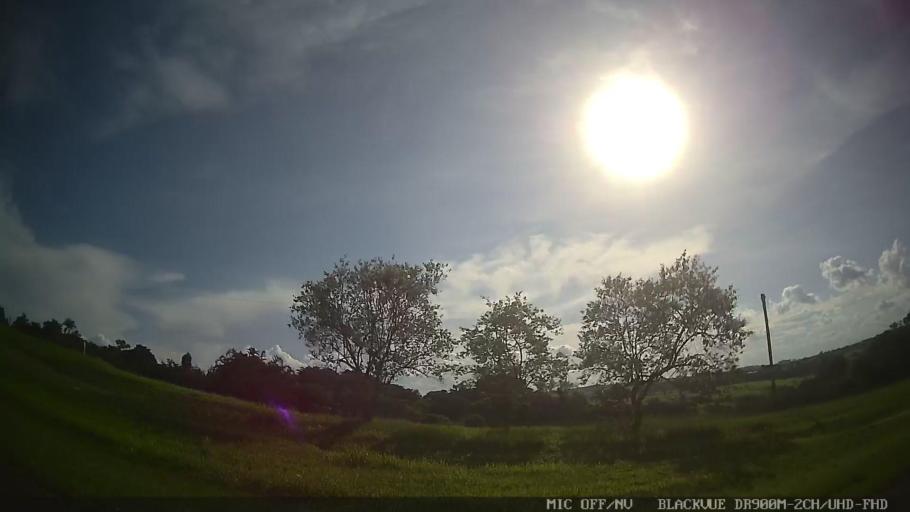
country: BR
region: Sao Paulo
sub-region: Tiete
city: Tiete
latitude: -23.1158
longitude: -47.7373
